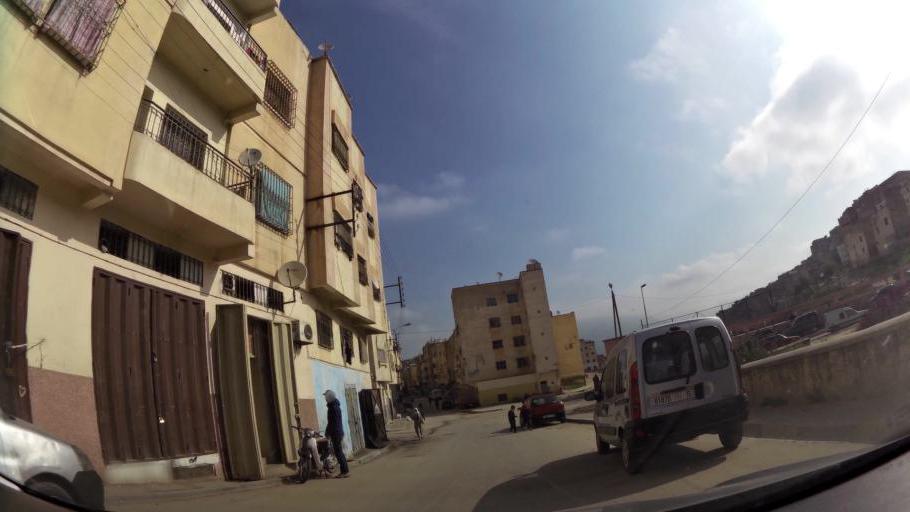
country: MA
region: Fes-Boulemane
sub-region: Fes
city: Fes
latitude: 34.0577
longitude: -4.9679
